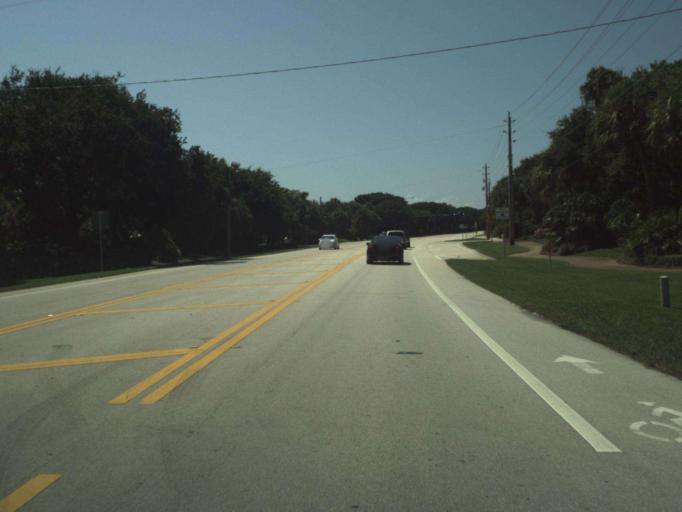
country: US
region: Florida
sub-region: Indian River County
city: South Beach
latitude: 27.6028
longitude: -80.3390
